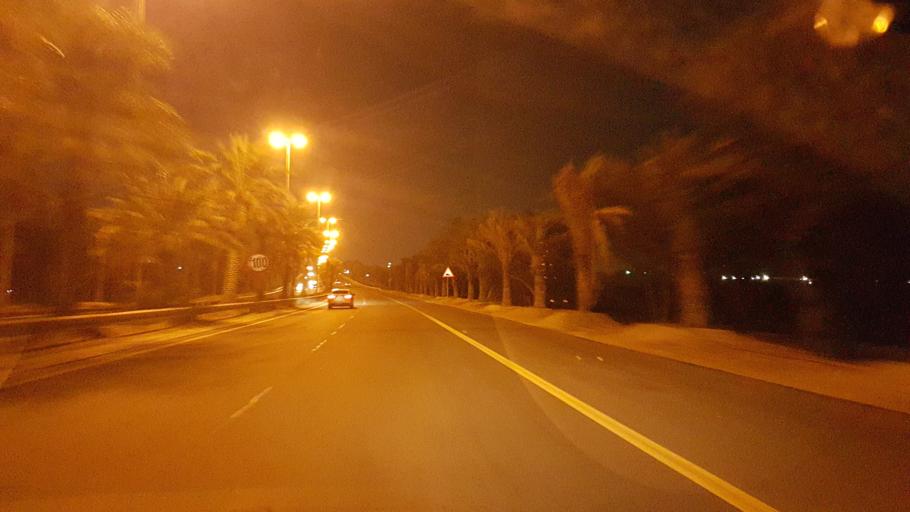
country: BH
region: Northern
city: Ar Rifa'
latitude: 26.1073
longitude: 50.5717
